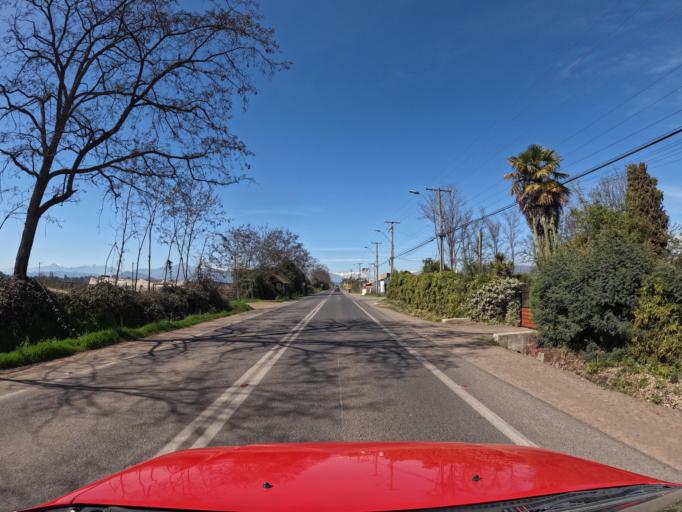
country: CL
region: Maule
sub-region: Provincia de Curico
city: Teno
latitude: -34.9649
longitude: -71.0497
